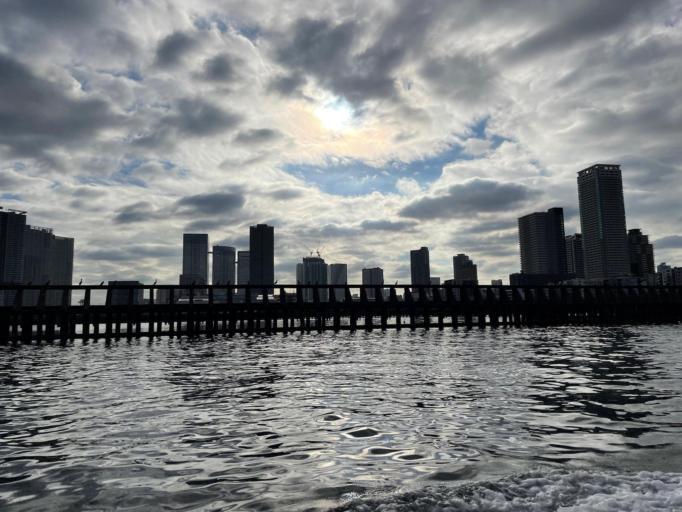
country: JP
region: Tokyo
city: Urayasu
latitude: 35.6646
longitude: 139.7922
